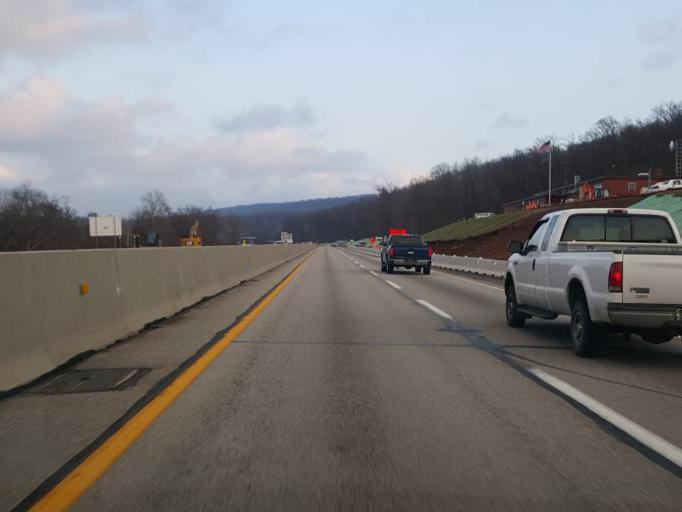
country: US
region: Pennsylvania
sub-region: Dauphin County
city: Steelton
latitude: 40.2021
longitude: -76.8442
